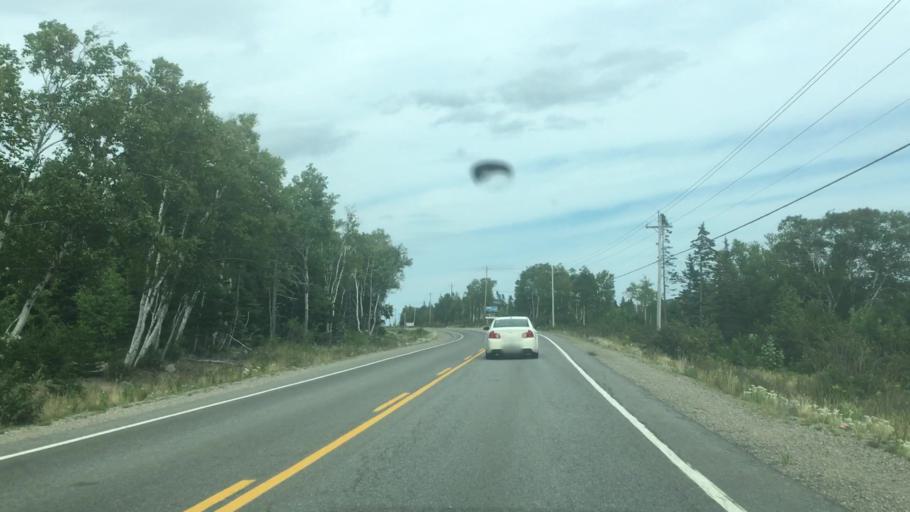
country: CA
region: Nova Scotia
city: Sydney Mines
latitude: 46.5172
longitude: -60.4255
